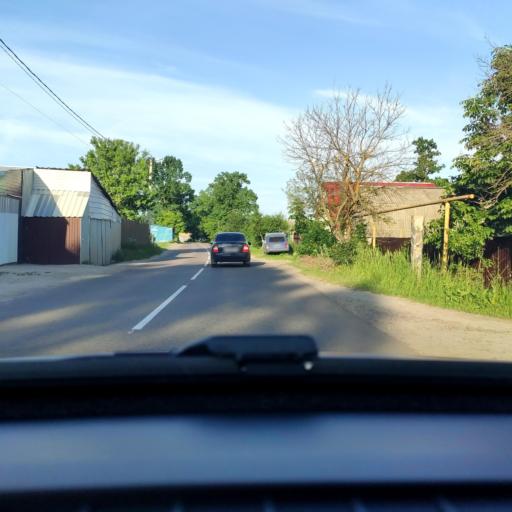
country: RU
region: Voronezj
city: Somovo
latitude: 51.7563
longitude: 39.4187
